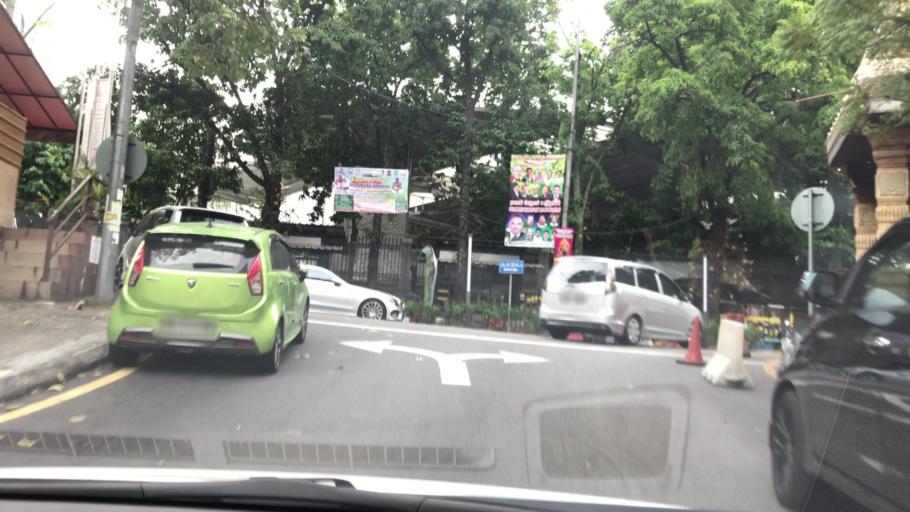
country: MY
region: Kuala Lumpur
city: Kuala Lumpur
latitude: 3.1465
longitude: 101.7004
